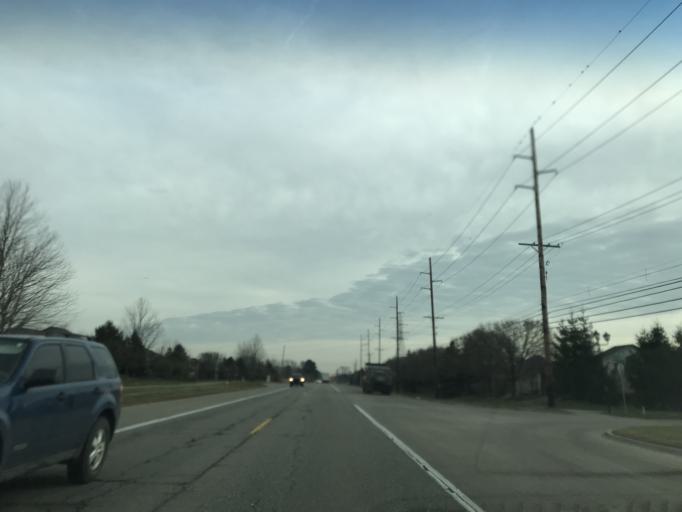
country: US
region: Michigan
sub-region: Macomb County
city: Mount Clemens
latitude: 42.6730
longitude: -82.9079
